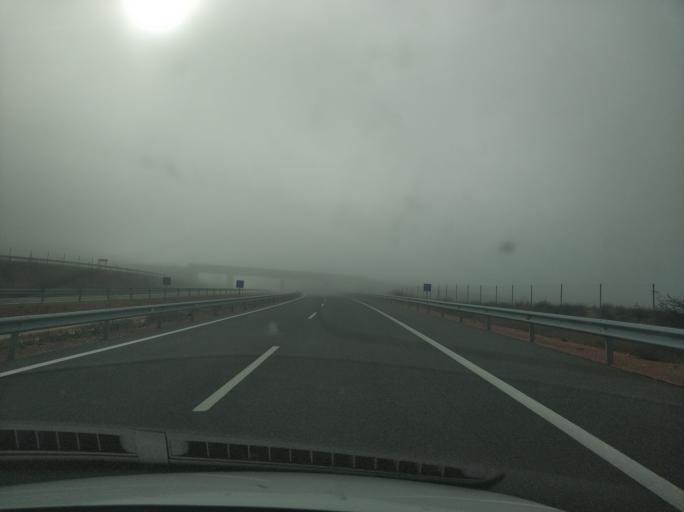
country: ES
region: Castille and Leon
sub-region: Provincia de Soria
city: Yelo
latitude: 41.2372
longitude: -2.4798
